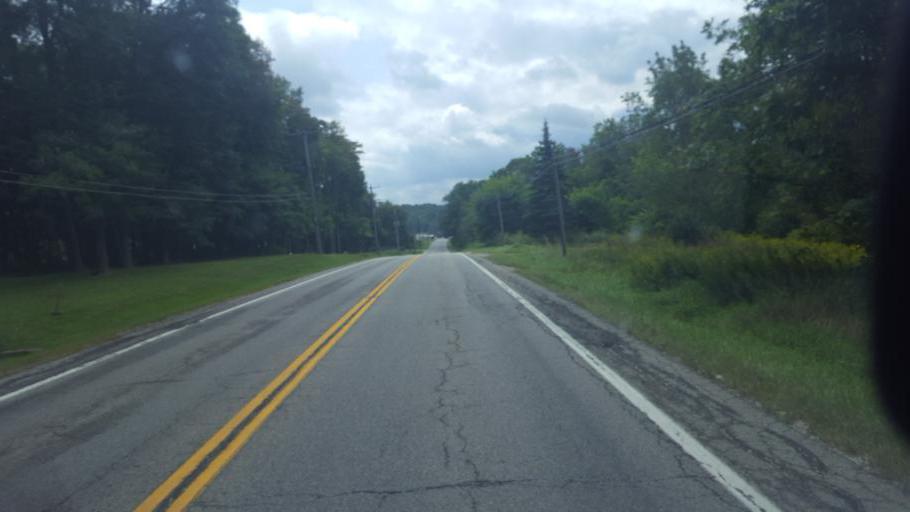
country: US
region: Ohio
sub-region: Geauga County
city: Burton
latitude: 41.5385
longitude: -81.1942
